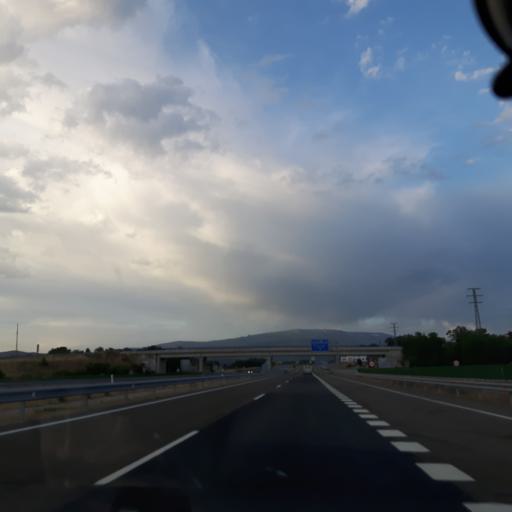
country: ES
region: Castille and Leon
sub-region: Provincia de Salamanca
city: Nava de Bejar
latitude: 40.4903
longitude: -5.6765
